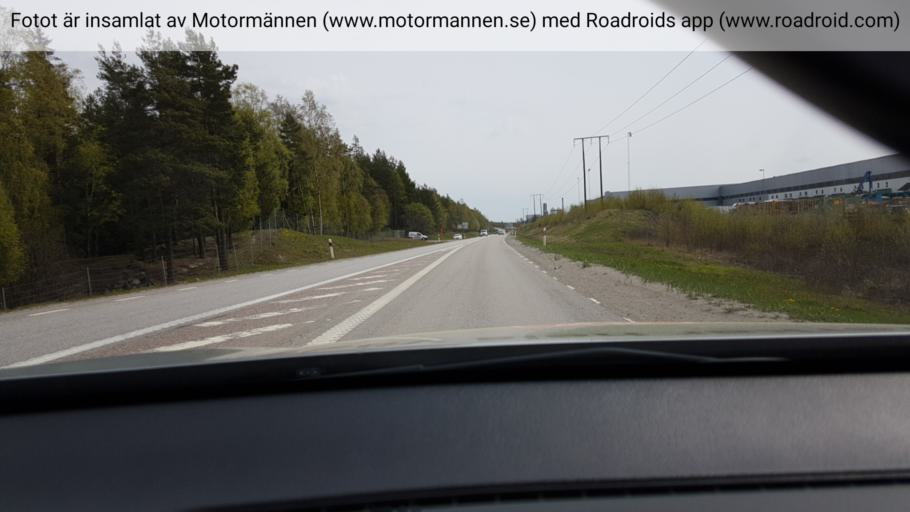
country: SE
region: Stockholm
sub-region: Haninge Kommun
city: Jordbro
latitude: 59.1596
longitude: 18.1127
